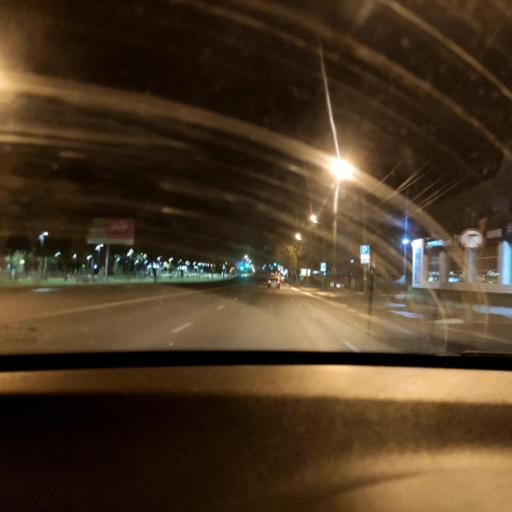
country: RU
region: Samara
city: Samara
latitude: 53.1944
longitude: 50.1905
